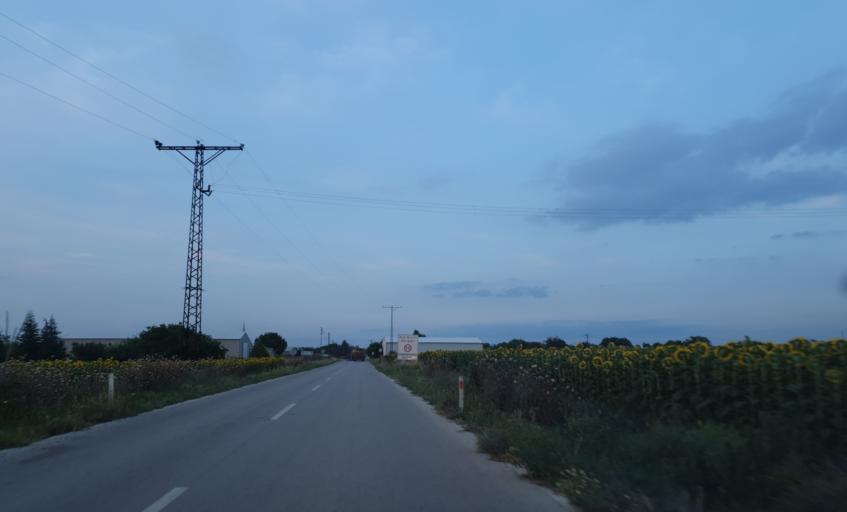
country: TR
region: Tekirdag
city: Beyazkoy
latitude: 41.4083
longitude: 27.6498
